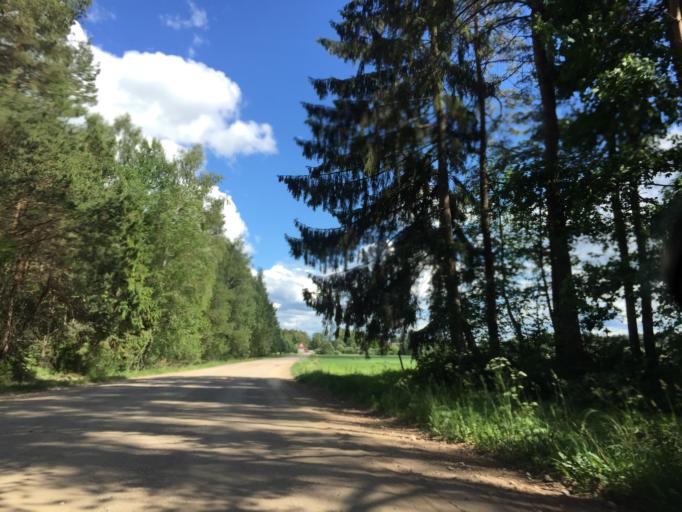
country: LT
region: Panevezys
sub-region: Birzai
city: Birzai
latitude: 56.3890
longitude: 24.6231
